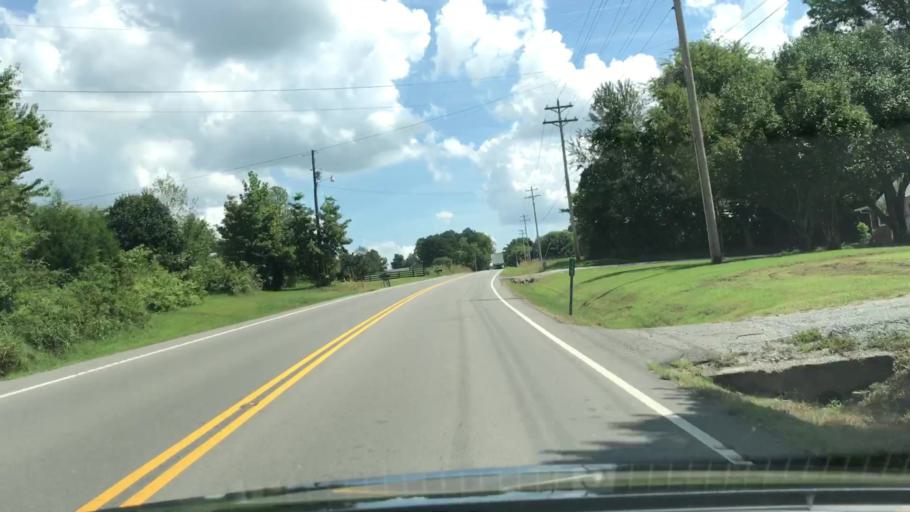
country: US
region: Tennessee
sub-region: Robertson County
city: Cross Plains
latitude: 36.5500
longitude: -86.7082
